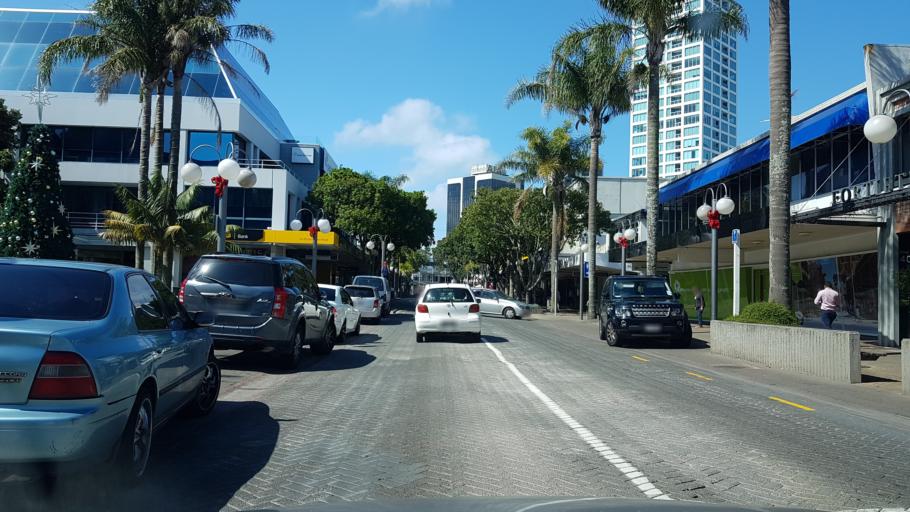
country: NZ
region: Auckland
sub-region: Auckland
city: North Shore
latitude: -36.7876
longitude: 174.7727
